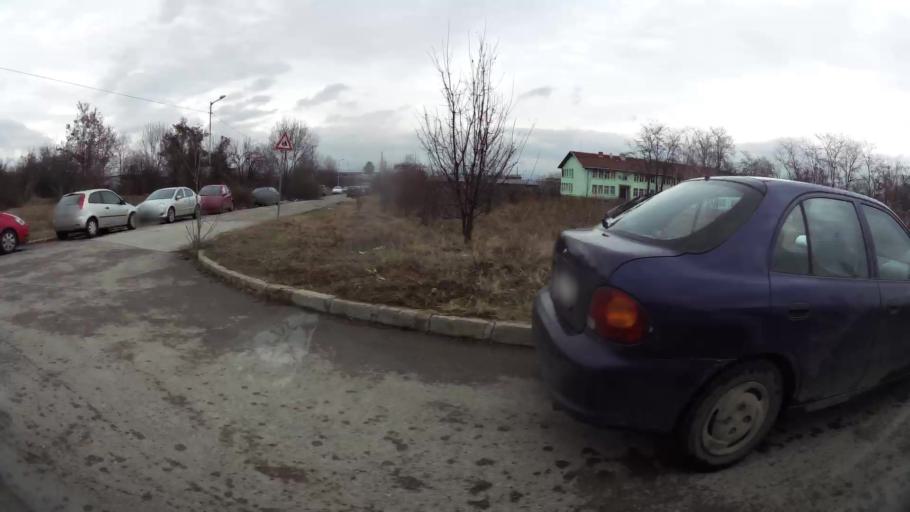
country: BG
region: Sofiya
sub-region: Obshtina Bozhurishte
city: Bozhurishte
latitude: 42.7266
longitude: 23.2583
